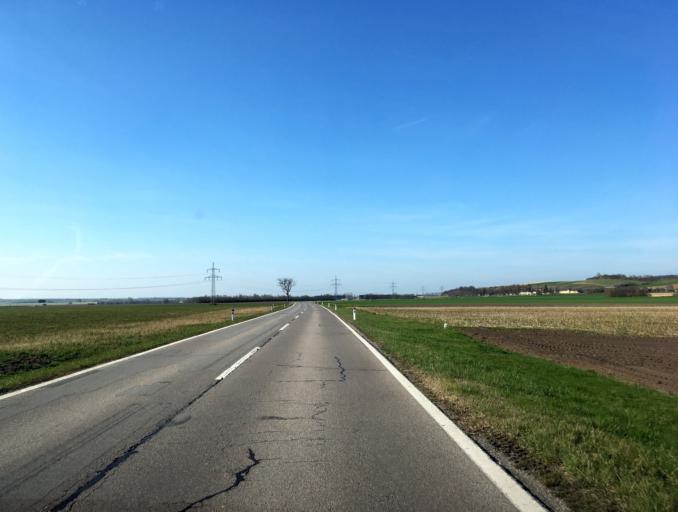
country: AT
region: Lower Austria
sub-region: Politischer Bezirk Bruck an der Leitha
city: Trautmannsdorf an der Leitha
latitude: 48.0503
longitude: 16.6191
